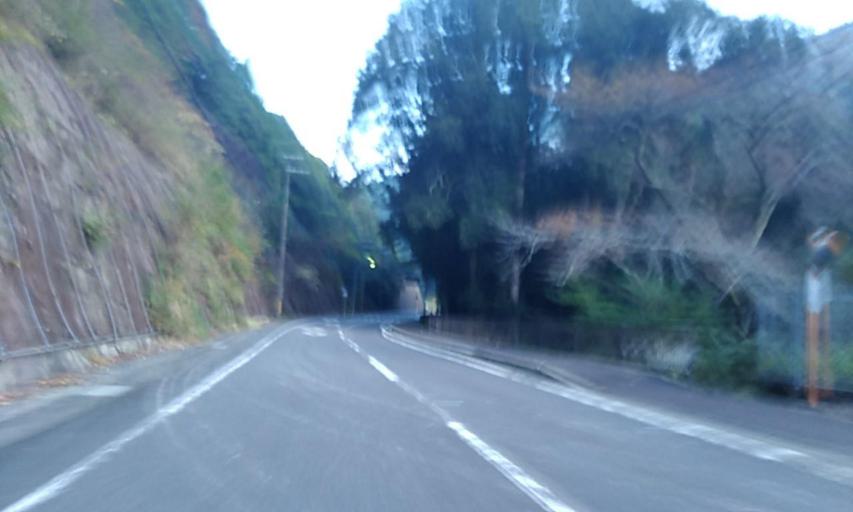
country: JP
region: Wakayama
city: Shingu
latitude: 33.7321
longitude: 135.9108
